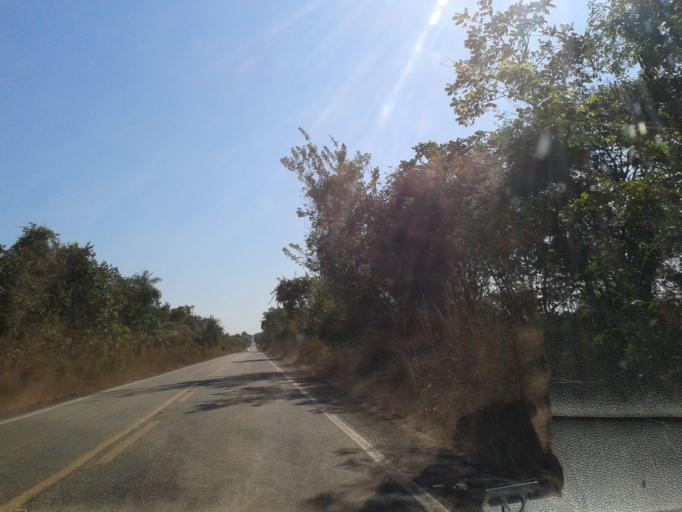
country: BR
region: Goias
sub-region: Mozarlandia
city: Mozarlandia
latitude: -14.6173
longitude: -50.5174
